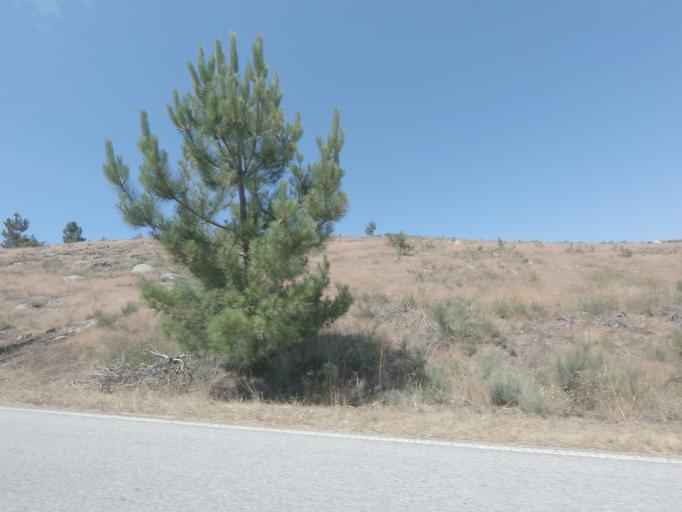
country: PT
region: Viseu
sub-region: Tarouca
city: Tarouca
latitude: 40.9832
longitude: -7.7938
